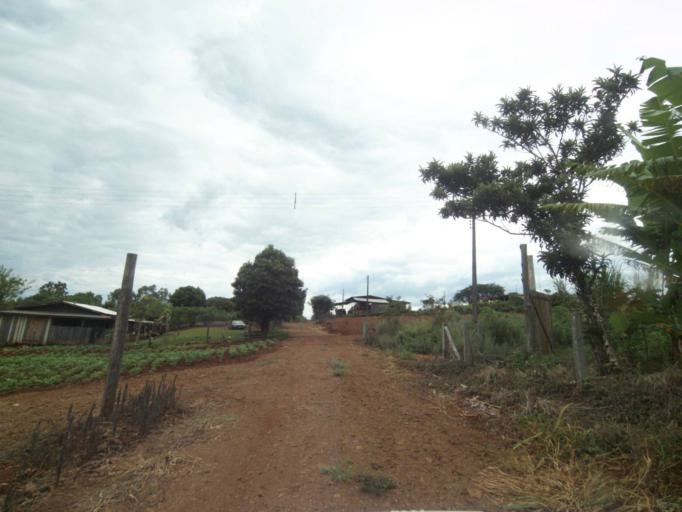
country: BR
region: Parana
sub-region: Guaraniacu
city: Guaraniacu
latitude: -24.9089
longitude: -52.9364
